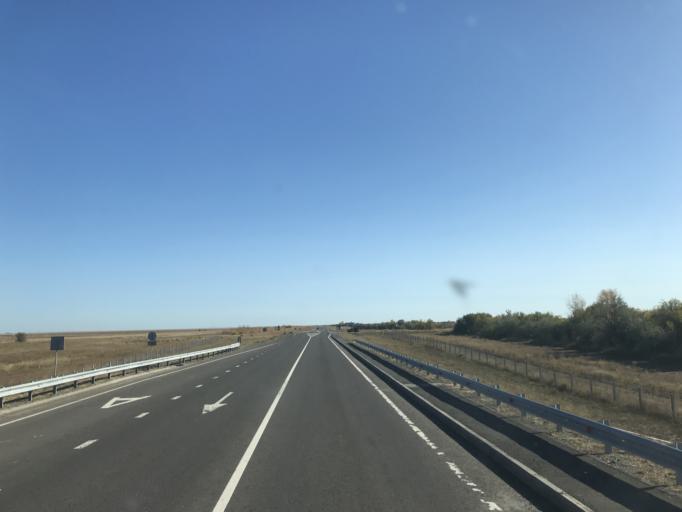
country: KZ
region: Pavlodar
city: Aksu
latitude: 52.0648
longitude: 77.1621
